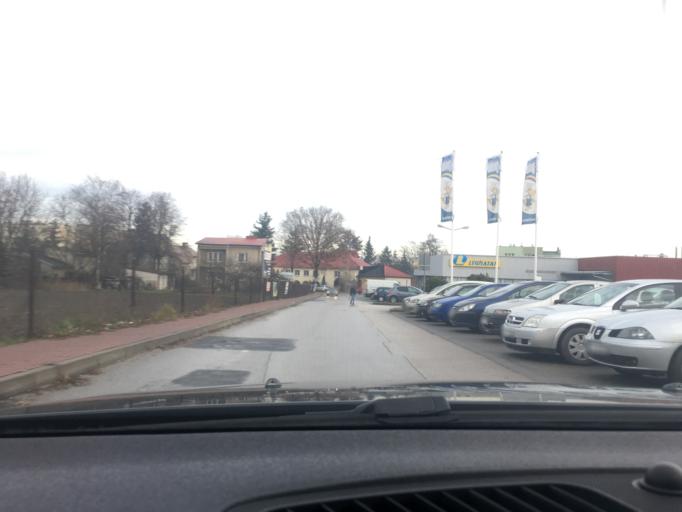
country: PL
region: Swietokrzyskie
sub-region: Powiat jedrzejowski
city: Jedrzejow
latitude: 50.6446
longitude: 20.2923
